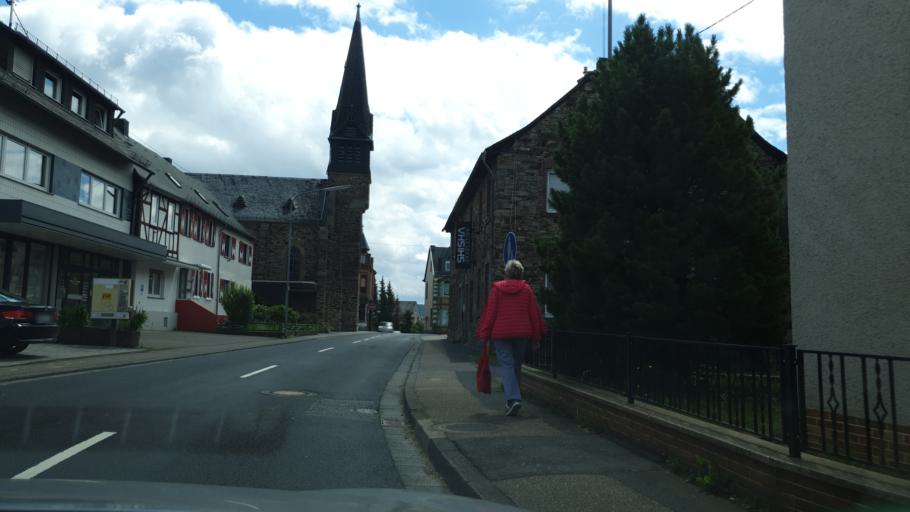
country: DE
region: Rheinland-Pfalz
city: Neuhausel
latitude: 50.3857
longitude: 7.7105
